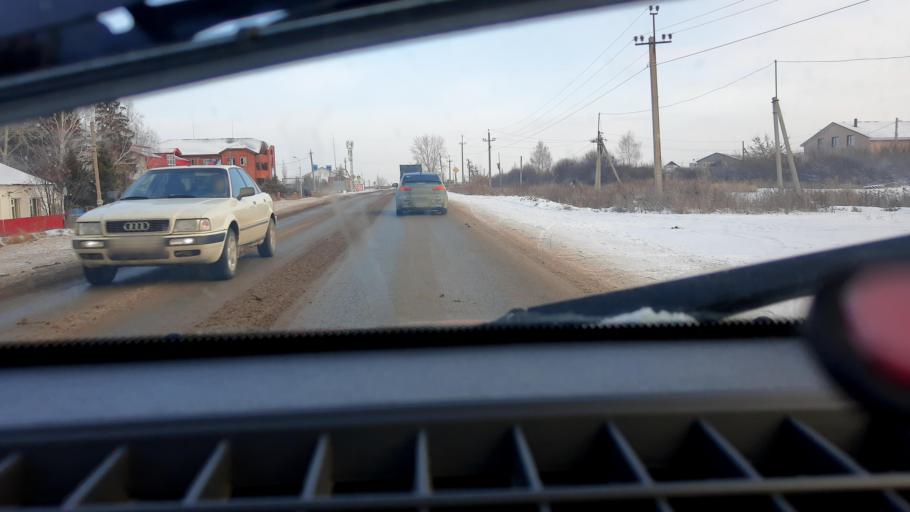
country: RU
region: Bashkortostan
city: Iglino
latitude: 54.7938
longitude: 56.2412
